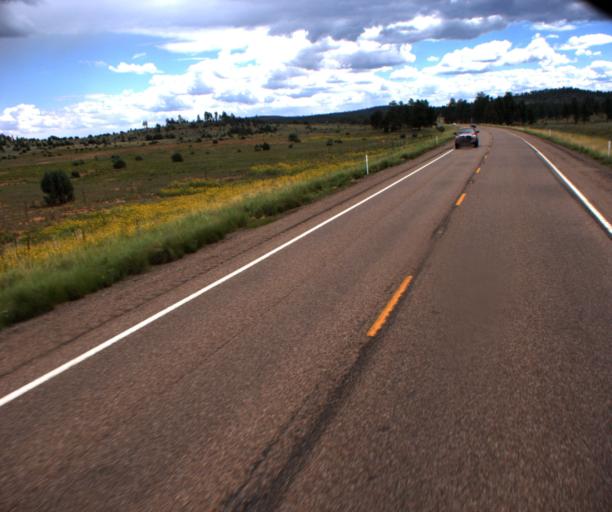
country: US
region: Arizona
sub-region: Navajo County
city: Linden
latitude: 34.3147
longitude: -110.2422
